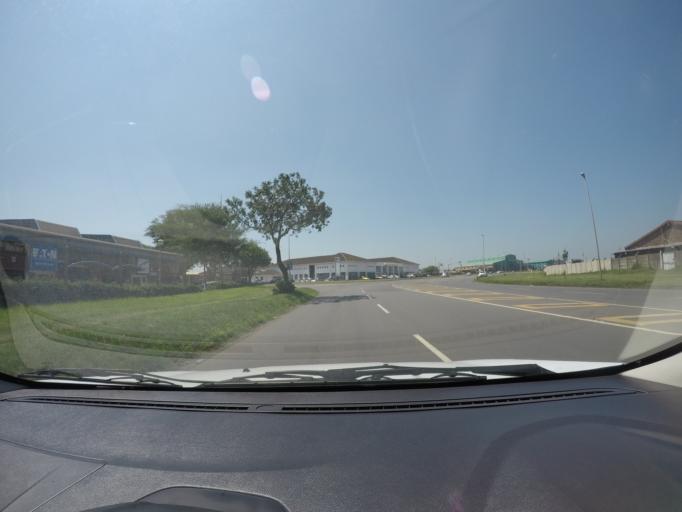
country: ZA
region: KwaZulu-Natal
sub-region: uThungulu District Municipality
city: Richards Bay
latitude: -28.7552
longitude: 32.0254
